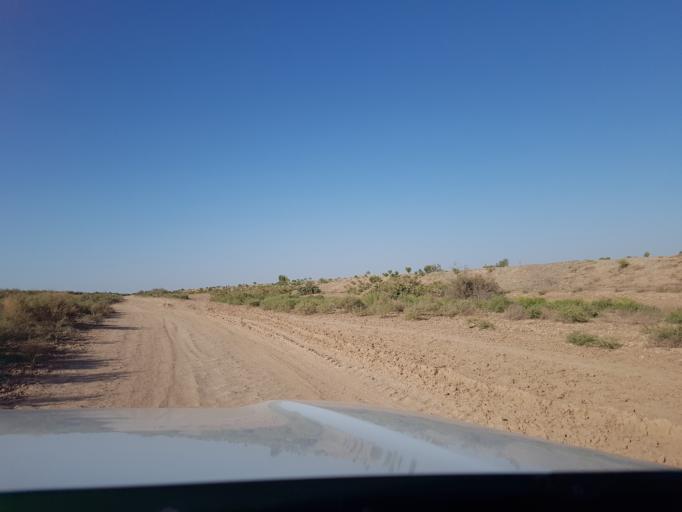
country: IR
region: Razavi Khorasan
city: Sarakhs
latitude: 36.9749
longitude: 61.3847
